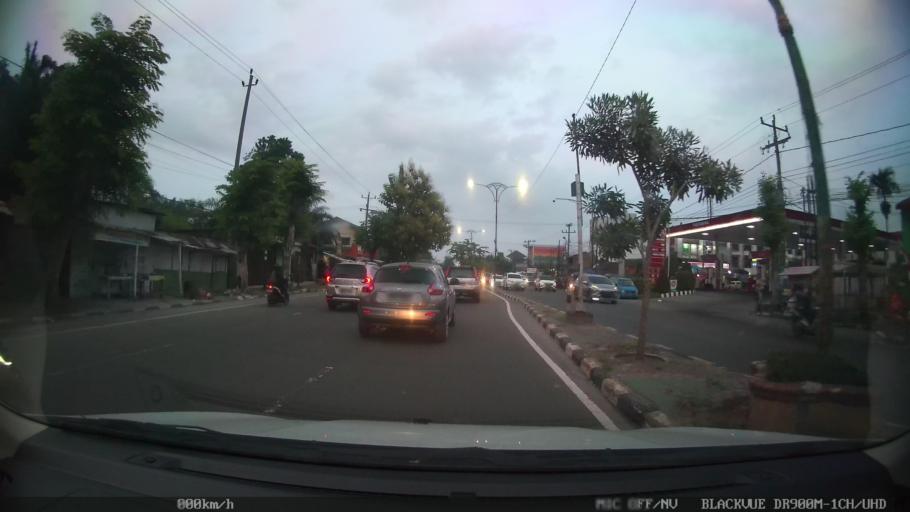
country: ID
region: North Sumatra
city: Sunggal
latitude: 3.5913
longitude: 98.6328
